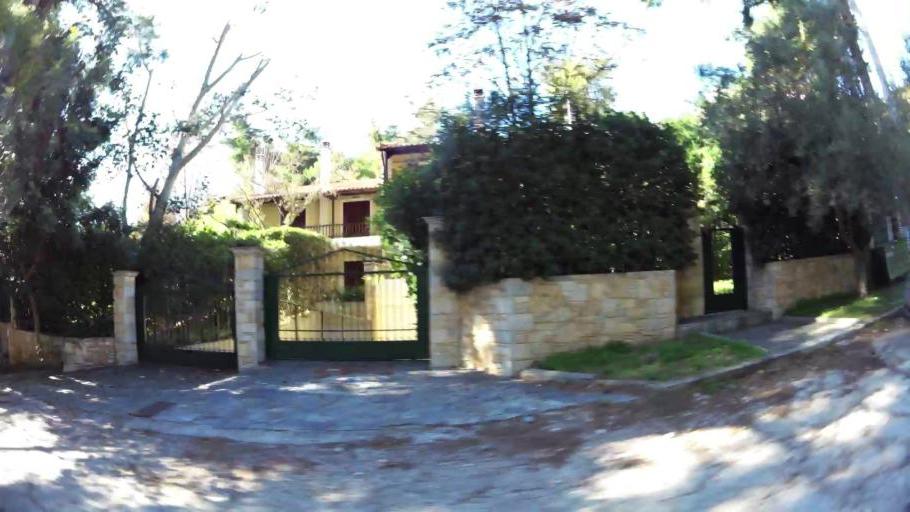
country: GR
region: Attica
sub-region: Nomarchia Anatolikis Attikis
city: Dionysos
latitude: 38.1040
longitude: 23.8922
